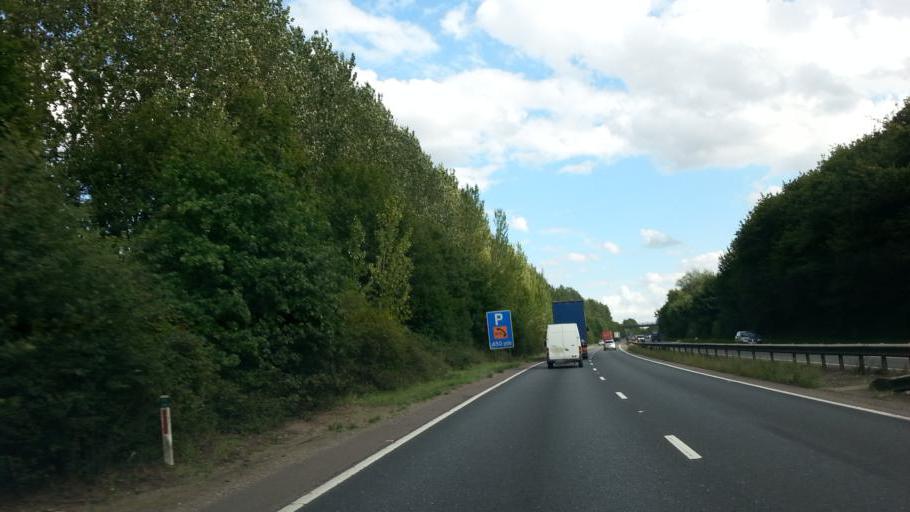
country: GB
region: England
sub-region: Suffolk
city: Thurston
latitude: 52.2371
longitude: 0.8359
